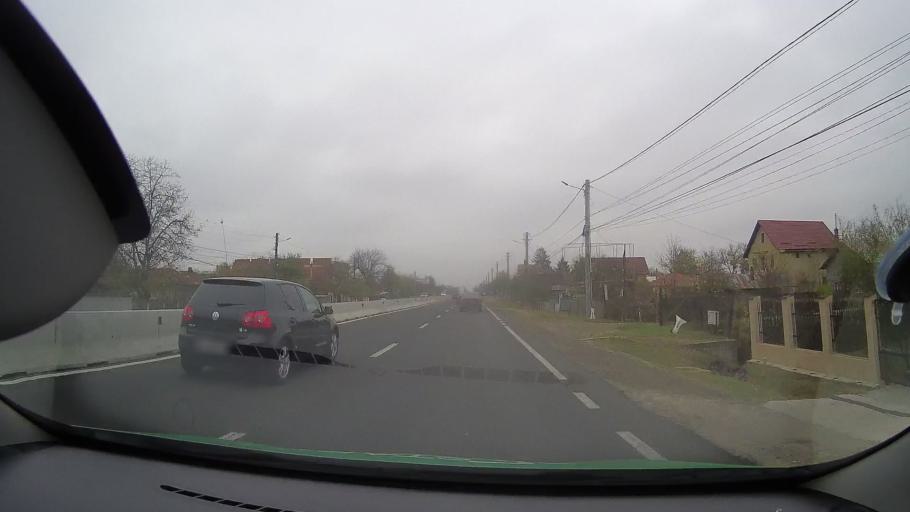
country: RO
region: Prahova
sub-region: Comuna Gorgota
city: Potigrafu
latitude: 44.7813
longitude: 26.0994
